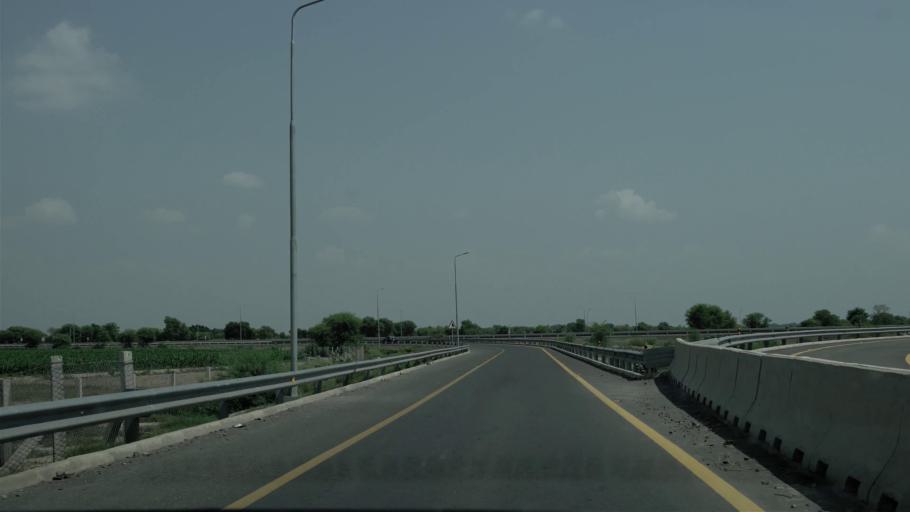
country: PK
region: Punjab
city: Gojra
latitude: 31.1845
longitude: 72.6418
